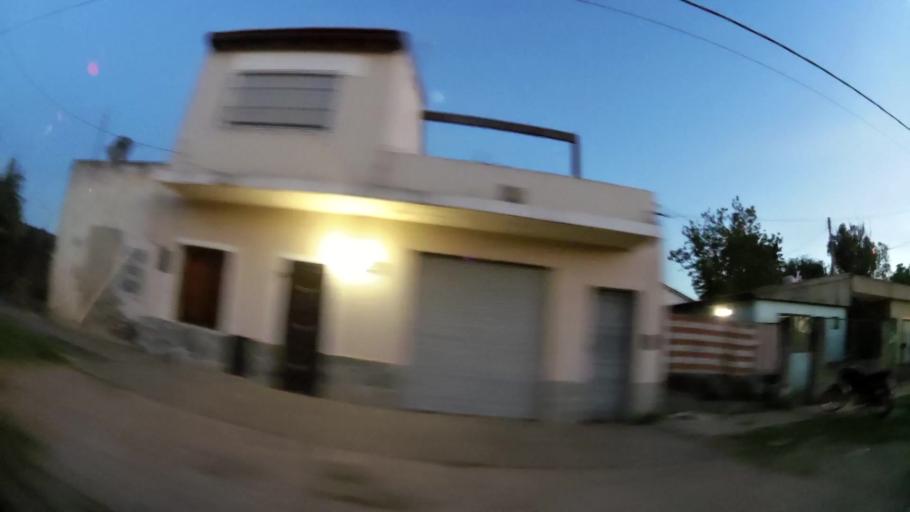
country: AR
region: Buenos Aires
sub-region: Partido de Quilmes
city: Quilmes
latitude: -34.7599
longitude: -58.1905
